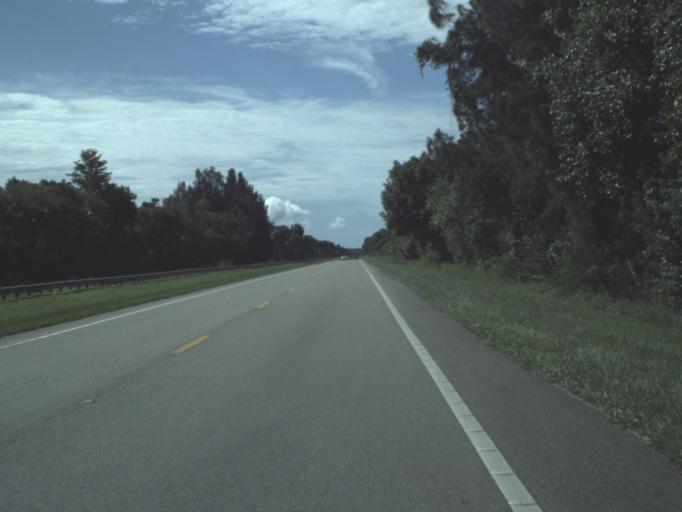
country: US
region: Florida
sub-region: Collier County
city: Immokalee
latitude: 26.2691
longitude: -81.3421
